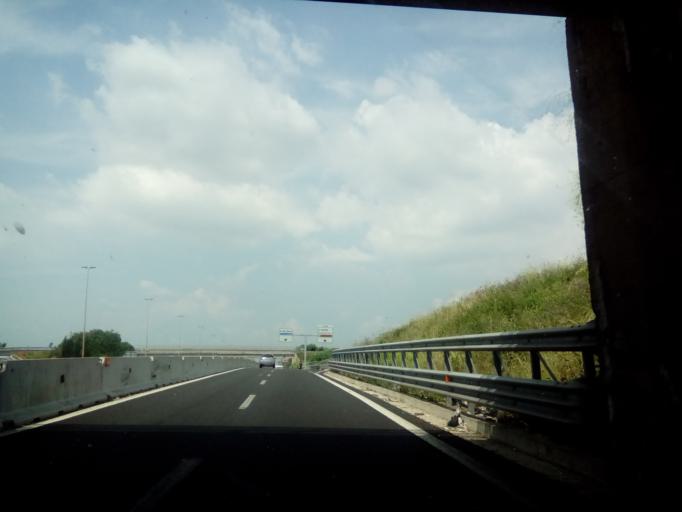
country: IT
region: Latium
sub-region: Citta metropolitana di Roma Capitale
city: Setteville
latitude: 41.8805
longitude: 12.6103
